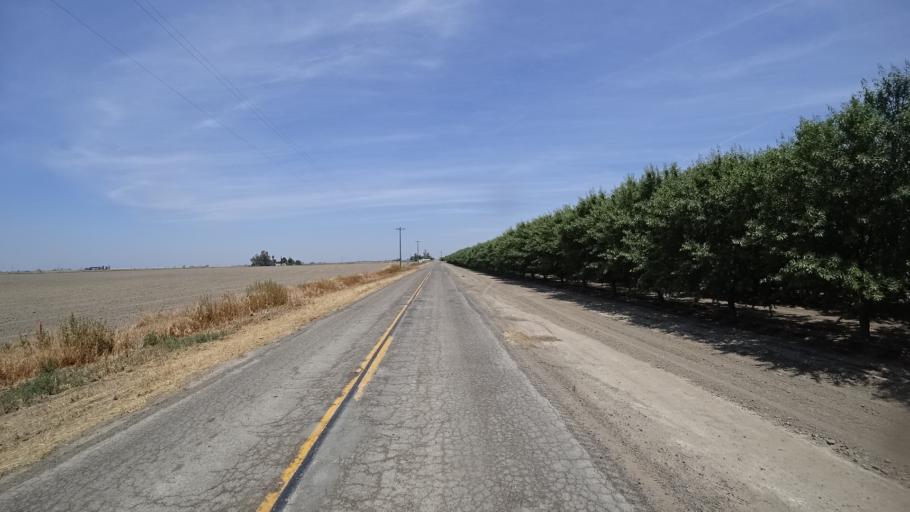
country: US
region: California
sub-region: Fresno County
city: Riverdale
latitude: 36.3883
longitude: -119.8962
